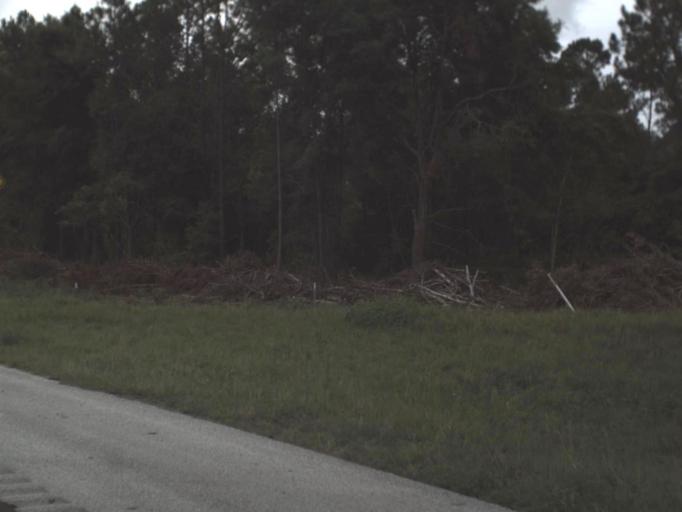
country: US
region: Florida
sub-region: Pasco County
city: San Antonio
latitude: 28.4180
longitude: -82.2926
